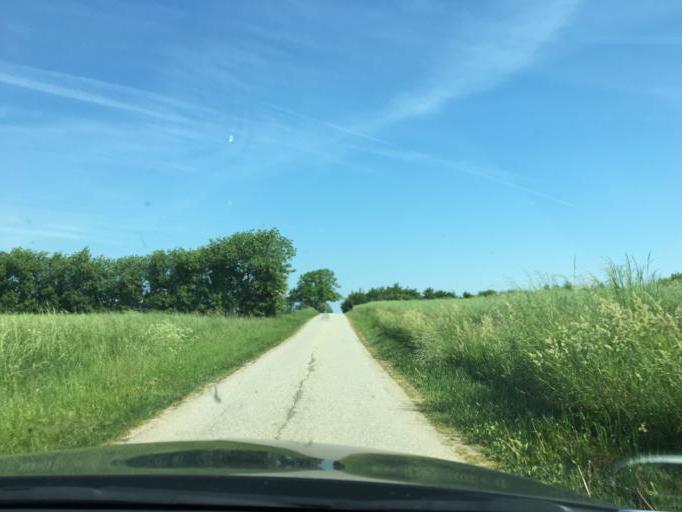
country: DK
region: South Denmark
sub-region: Kolding Kommune
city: Kolding
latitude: 55.5505
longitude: 9.4699
